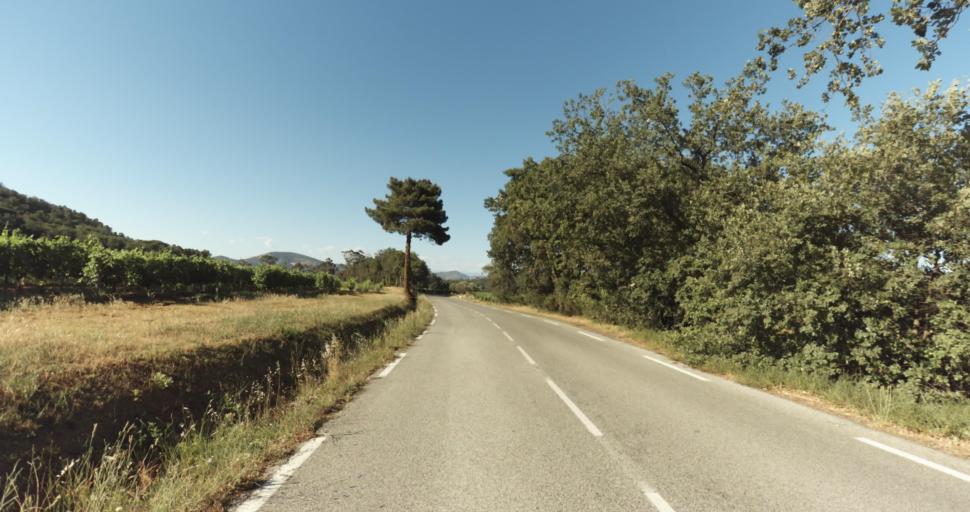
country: FR
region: Provence-Alpes-Cote d'Azur
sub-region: Departement du Var
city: Gassin
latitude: 43.2435
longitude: 6.5889
